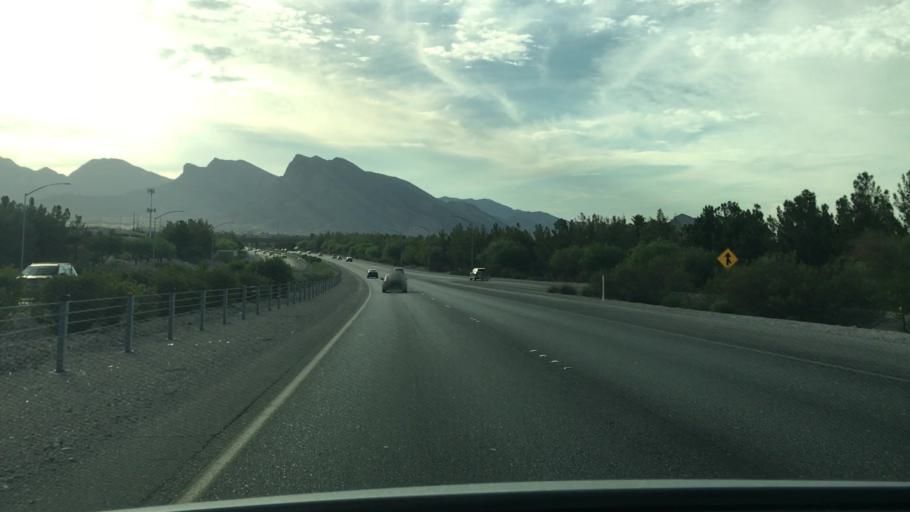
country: US
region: Nevada
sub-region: Clark County
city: Summerlin South
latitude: 36.1890
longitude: -115.3095
